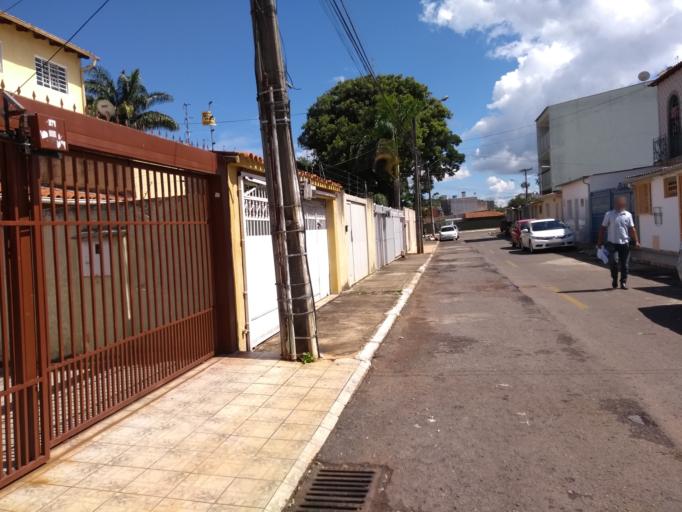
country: BR
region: Federal District
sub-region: Brasilia
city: Brasilia
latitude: -15.7899
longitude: -47.9404
